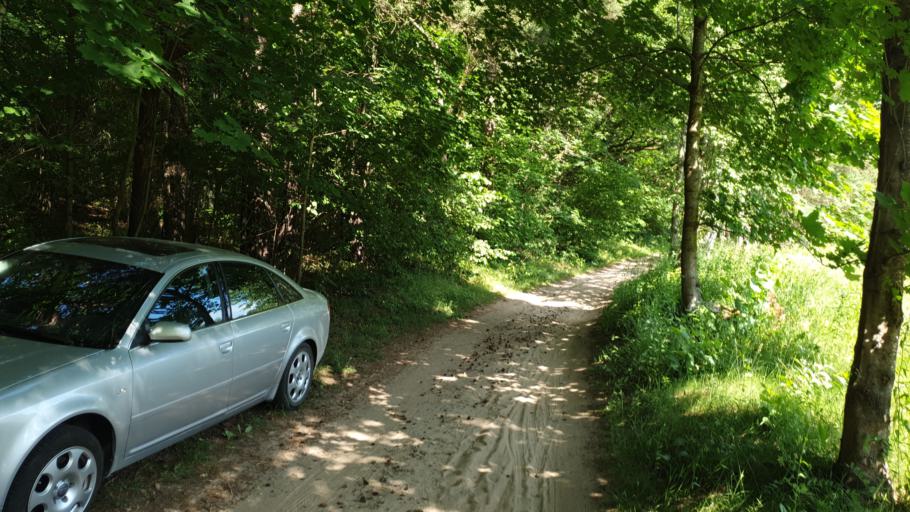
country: LT
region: Vilnius County
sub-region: Vilnius
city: Fabijoniskes
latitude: 54.7879
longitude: 25.3181
